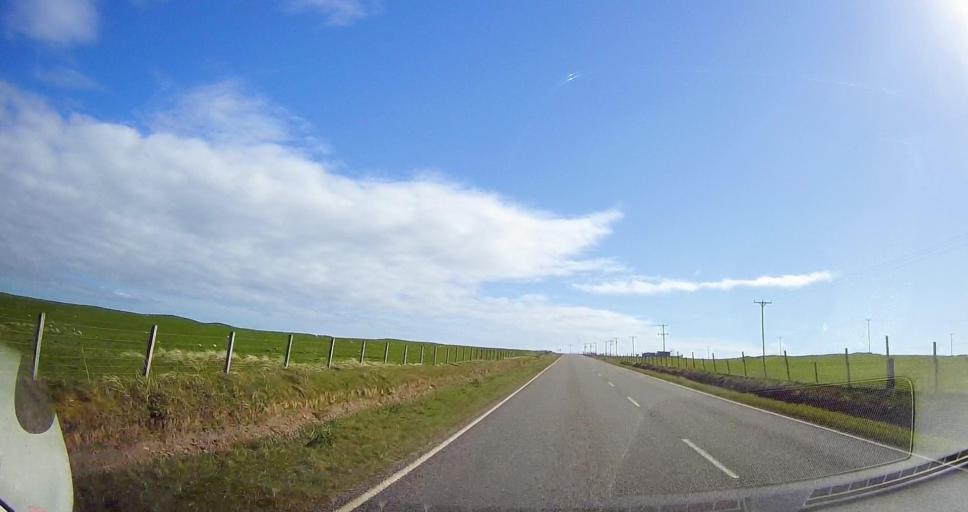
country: GB
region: Scotland
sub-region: Shetland Islands
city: Sandwick
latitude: 59.9018
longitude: -1.3028
